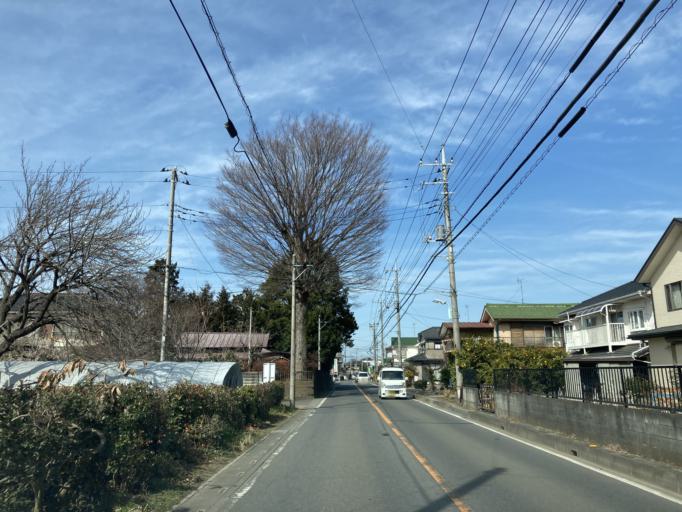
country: JP
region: Saitama
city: Tokorozawa
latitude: 35.8206
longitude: 139.4772
